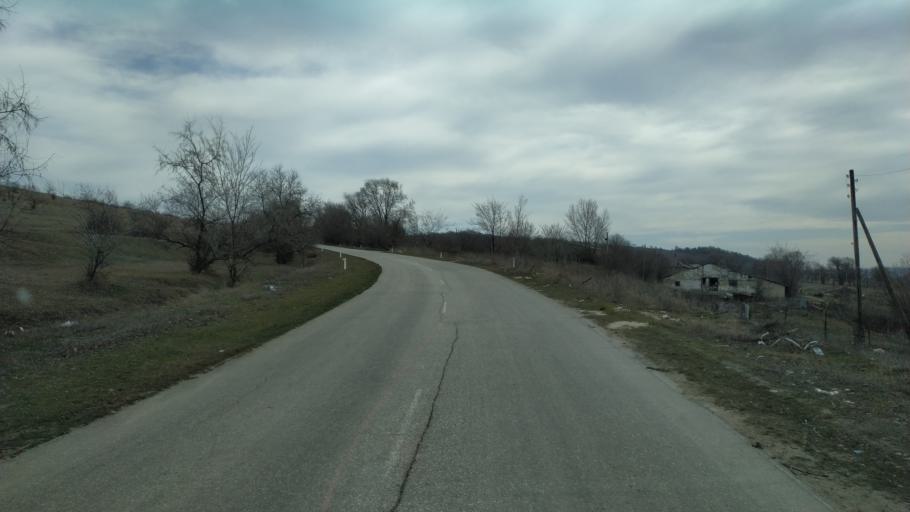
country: MD
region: Nisporeni
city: Nisporeni
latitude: 46.9559
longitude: 28.2220
